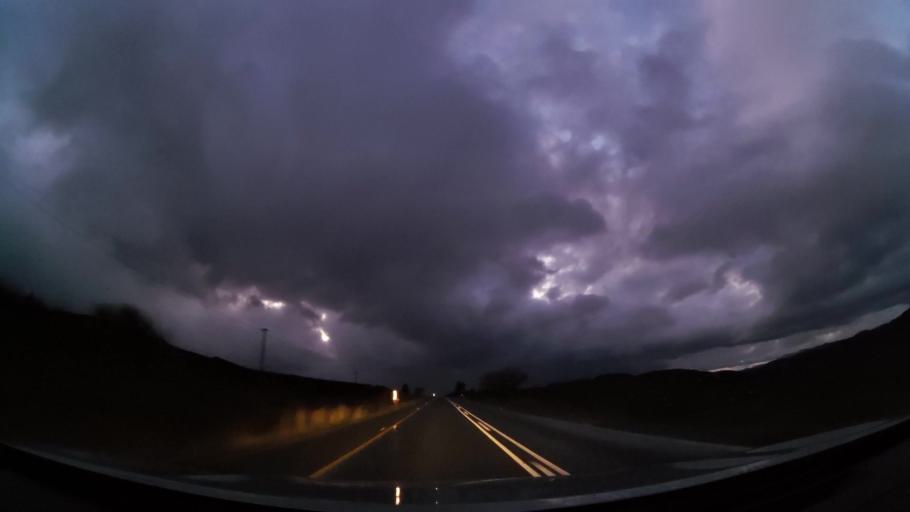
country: ZA
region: Western Cape
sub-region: Overberg District Municipality
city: Swellendam
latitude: -33.9058
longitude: 20.4001
